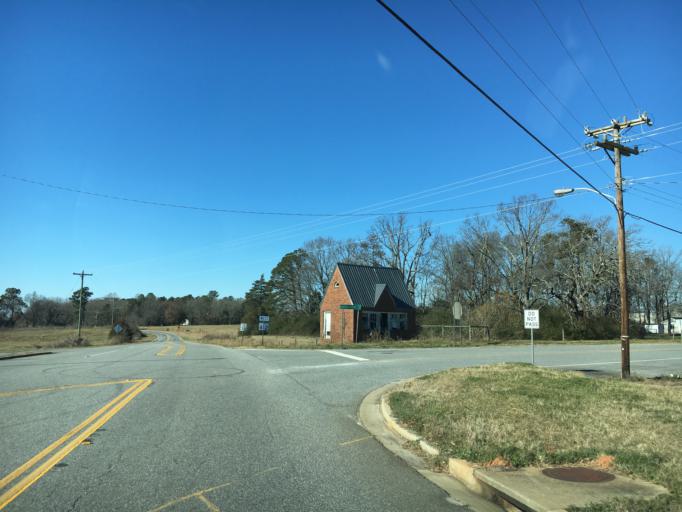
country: US
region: South Carolina
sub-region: Anderson County
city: Iva
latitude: 34.3769
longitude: -82.6957
